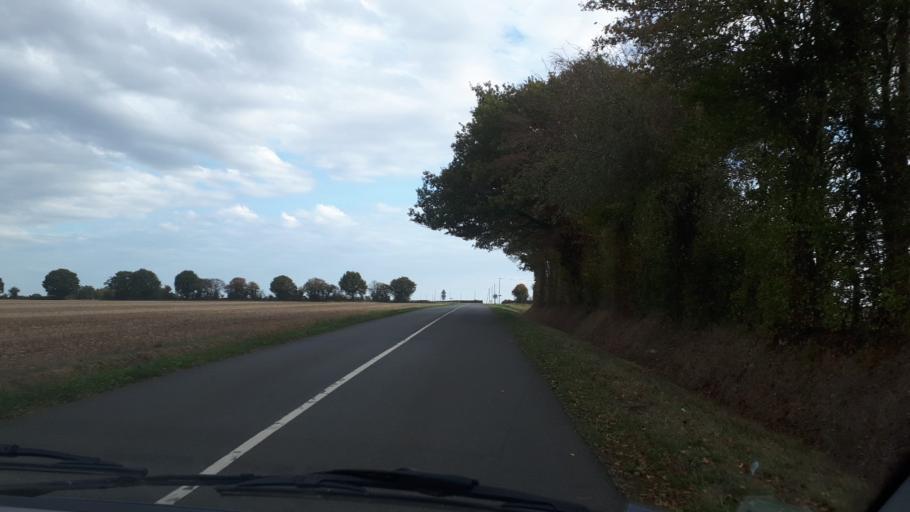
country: FR
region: Centre
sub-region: Departement du Loir-et-Cher
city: Mondoubleau
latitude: 48.0041
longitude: 0.9155
